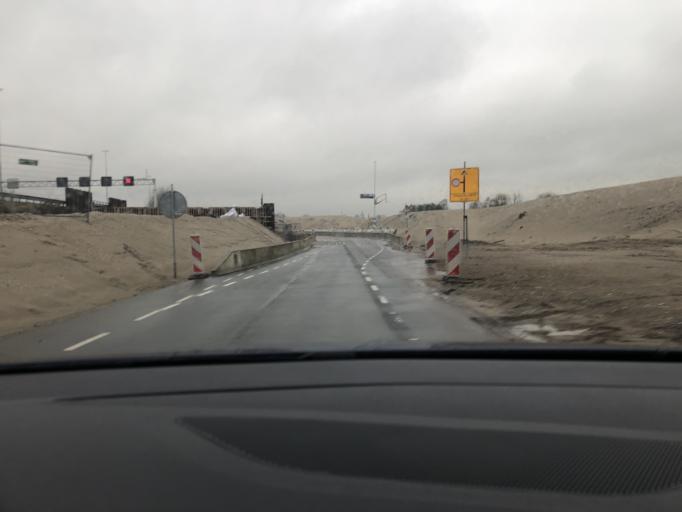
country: NL
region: South Holland
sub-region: Gemeente Schiedam
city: Schiedam
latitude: 51.9597
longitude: 4.4093
